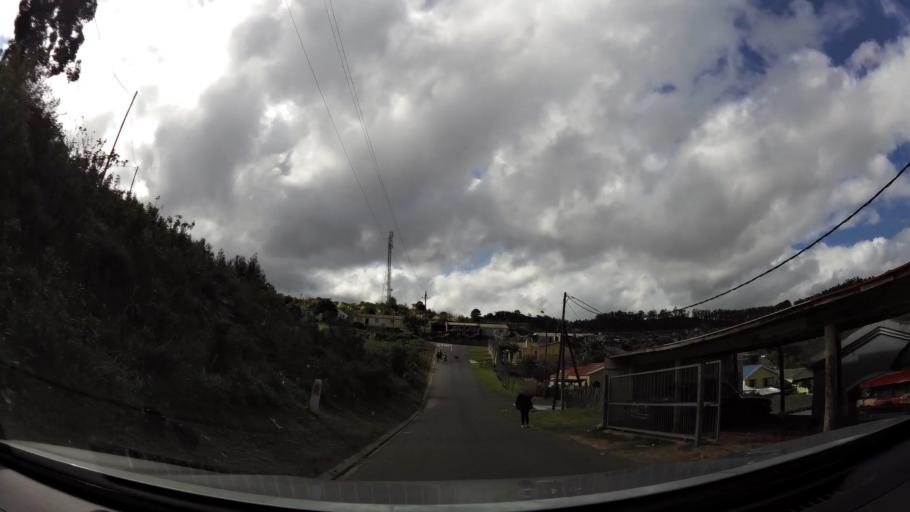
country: ZA
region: Western Cape
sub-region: Eden District Municipality
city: Knysna
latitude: -34.0541
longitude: 23.0957
